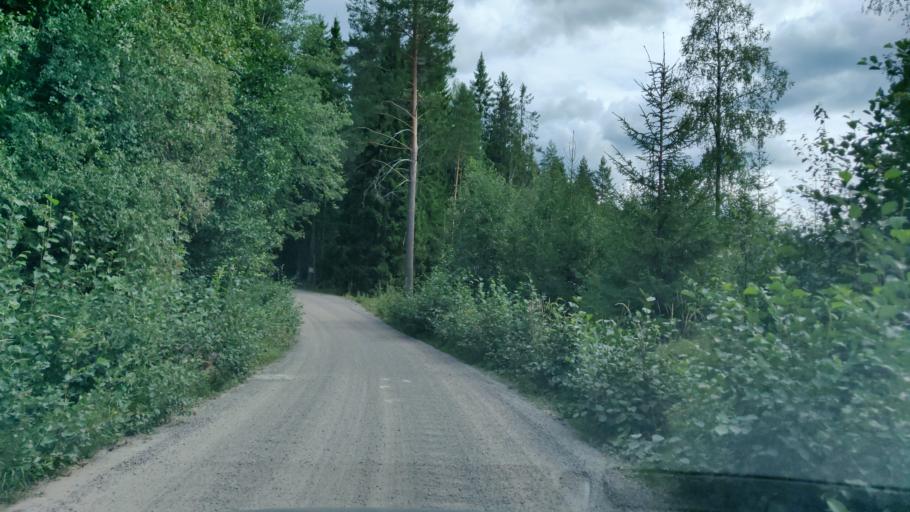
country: SE
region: Vaermland
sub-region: Hagfors Kommun
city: Hagfors
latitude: 60.0061
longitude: 13.7143
